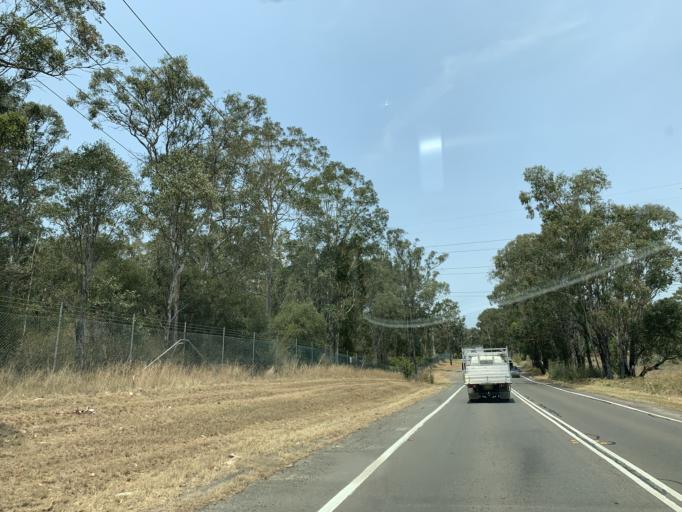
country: AU
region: New South Wales
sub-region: Fairfield
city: Horsley Park
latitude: -33.8325
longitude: 150.8739
